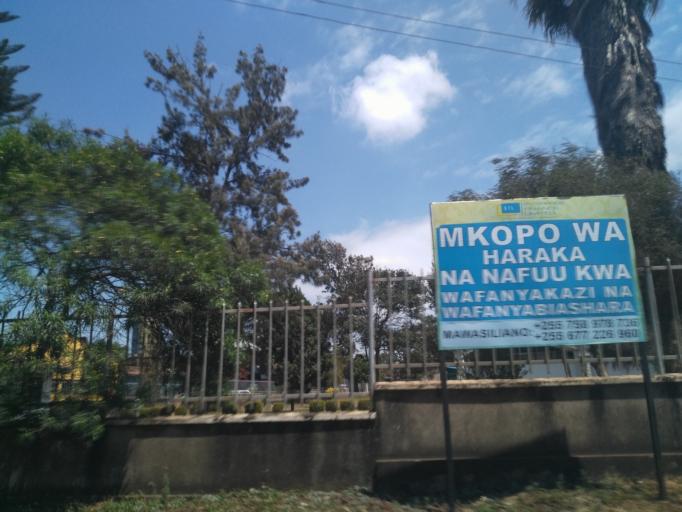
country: TZ
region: Arusha
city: Arusha
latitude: -3.3696
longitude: 36.6877
